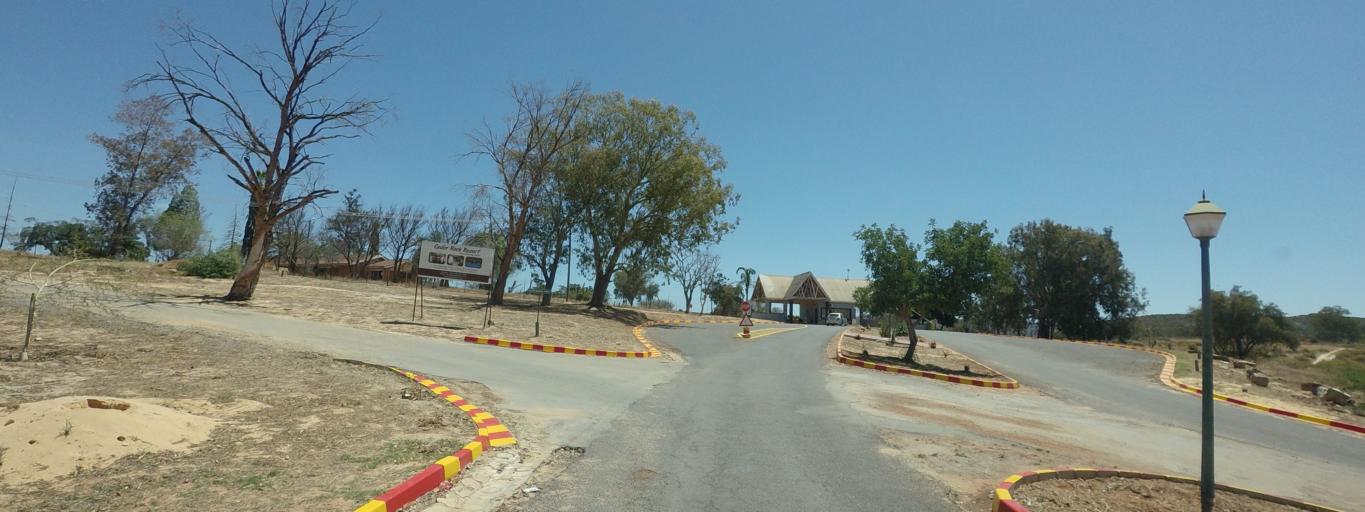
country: ZA
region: Western Cape
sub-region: West Coast District Municipality
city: Clanwilliam
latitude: -32.1902
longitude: 18.8871
